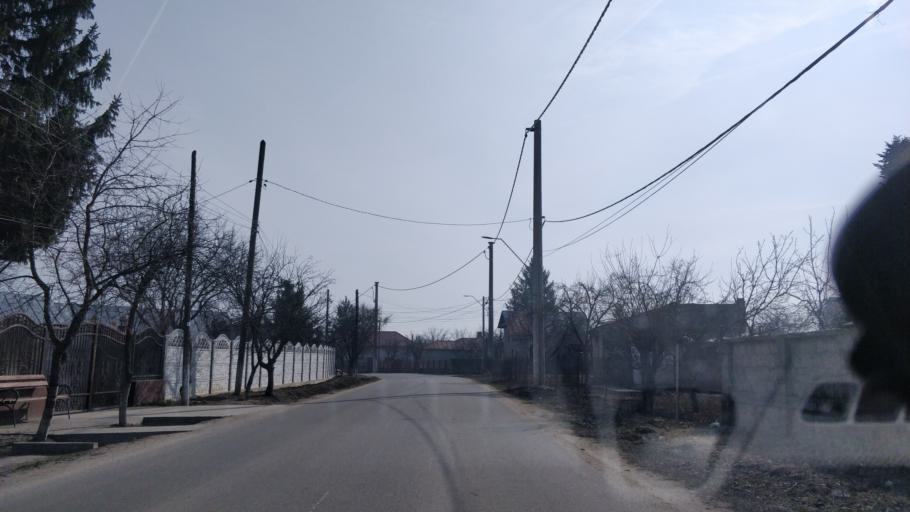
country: RO
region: Giurgiu
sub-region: Comuna Ulmi
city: Ulmi
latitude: 44.4840
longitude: 25.7935
